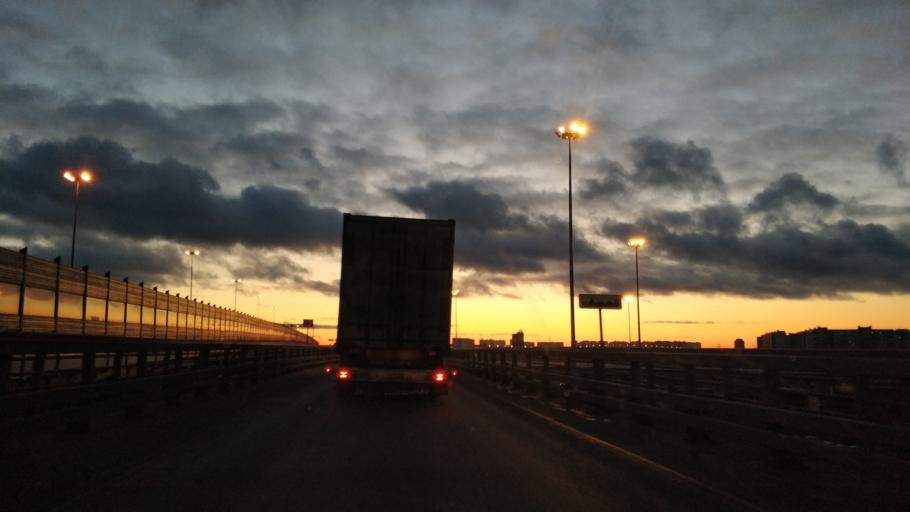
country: RU
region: St.-Petersburg
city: Obukhovo
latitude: 59.8337
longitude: 30.4459
